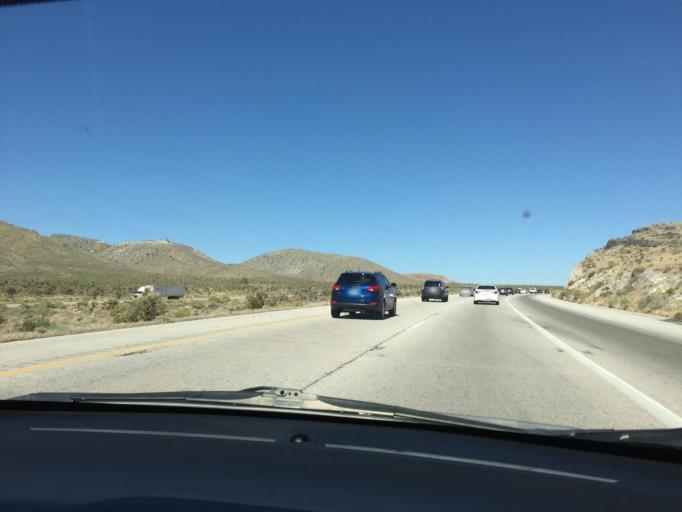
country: US
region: Nevada
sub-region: Clark County
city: Sandy Valley
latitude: 35.4746
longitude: -115.5739
